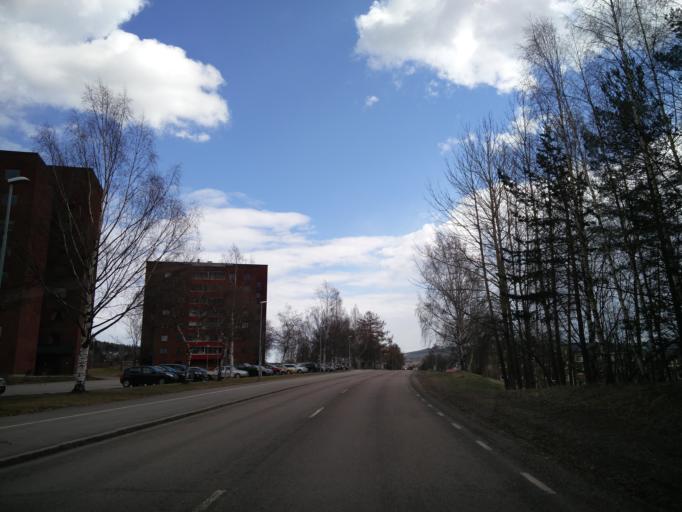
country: SE
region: Vaesternorrland
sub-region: Sundsvalls Kommun
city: Sundsvall
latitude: 62.4038
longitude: 17.2504
